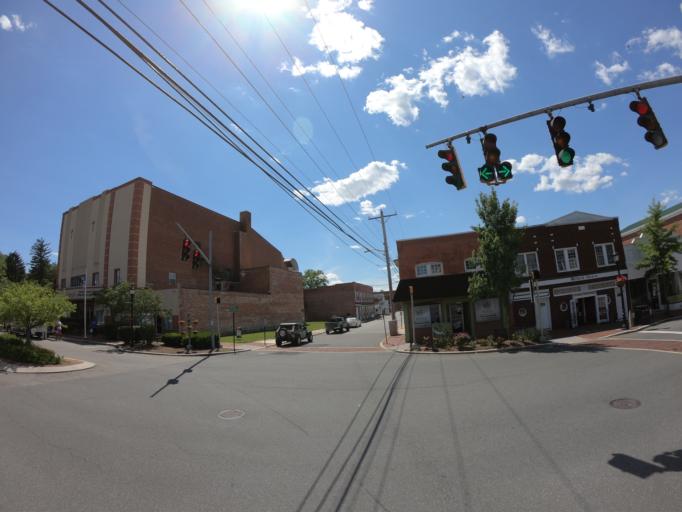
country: US
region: Delaware
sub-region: Sussex County
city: Milford
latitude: 38.9126
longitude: -75.4283
